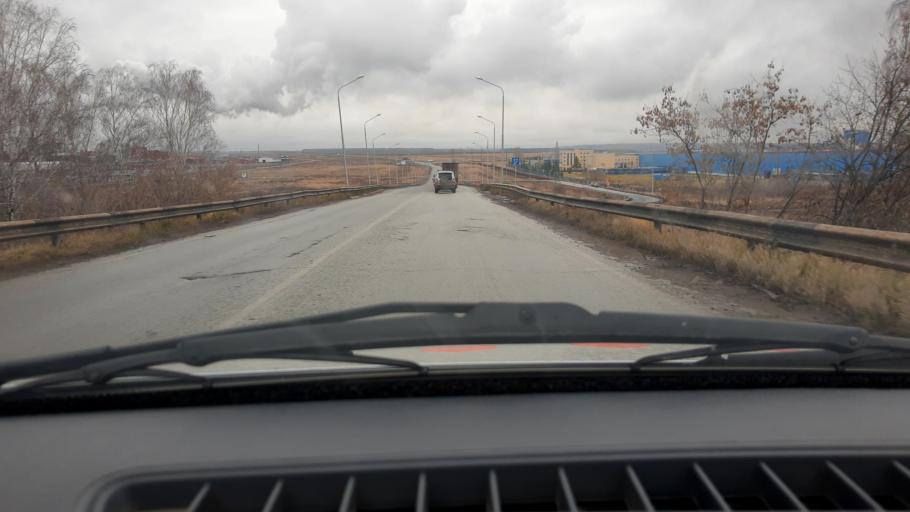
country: RU
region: Bashkortostan
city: Iglino
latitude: 54.7739
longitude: 56.2570
